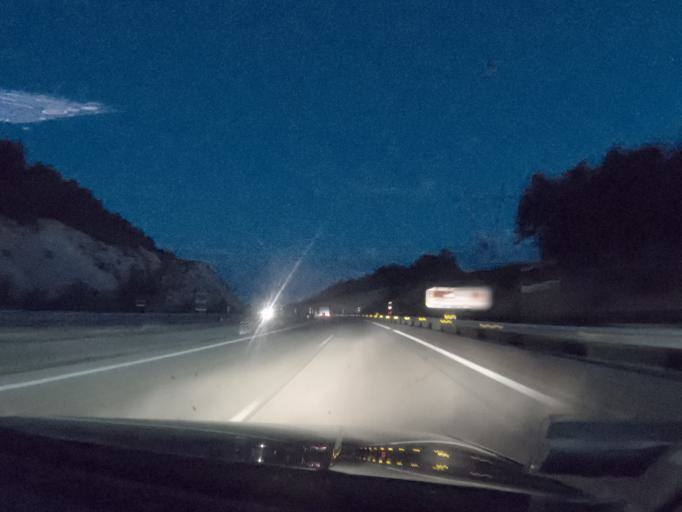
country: ES
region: Castille and Leon
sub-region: Provincia de Leon
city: Villagaton
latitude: 42.5672
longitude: -6.2145
